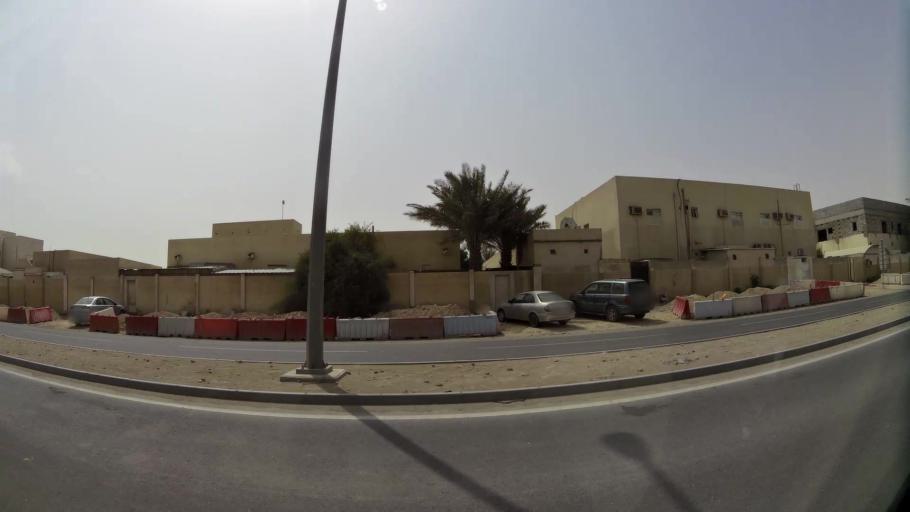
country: QA
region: Baladiyat ar Rayyan
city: Ar Rayyan
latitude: 25.2306
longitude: 51.3848
